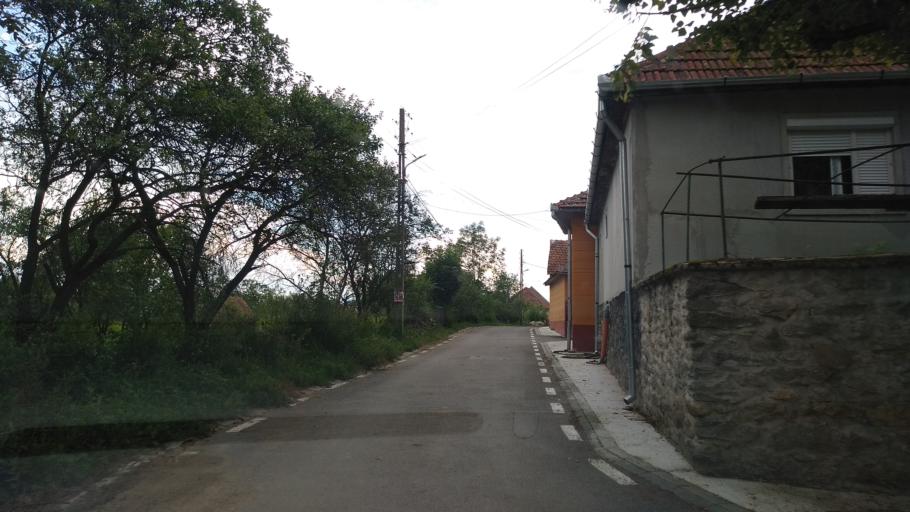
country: RO
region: Hunedoara
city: Salasu de Sus
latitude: 45.4947
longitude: 22.9685
